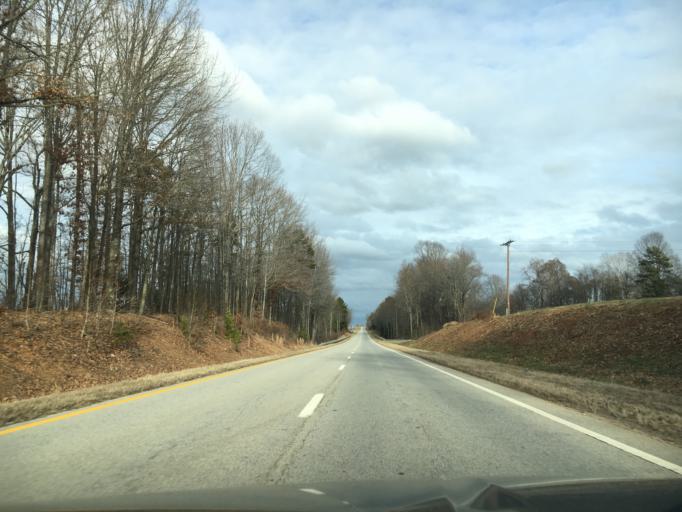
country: US
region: Virginia
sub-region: Lunenburg County
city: Victoria
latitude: 37.1451
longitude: -78.2963
